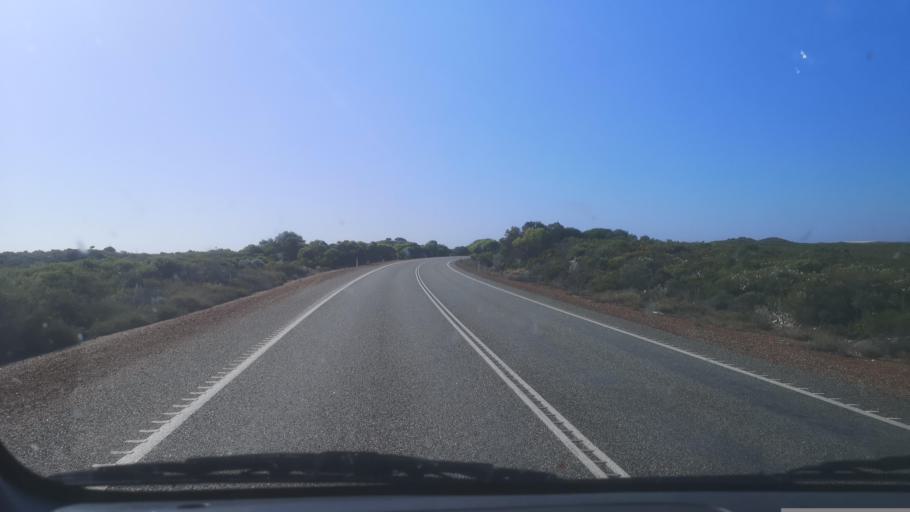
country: AU
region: Western Australia
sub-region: Dandaragan
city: Jurien Bay
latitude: -30.7882
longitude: 115.2101
